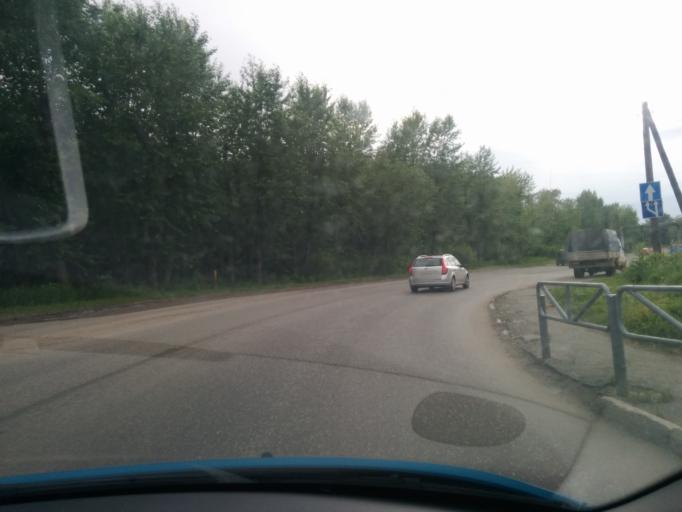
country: RU
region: Perm
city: Perm
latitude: 58.0025
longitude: 56.1933
